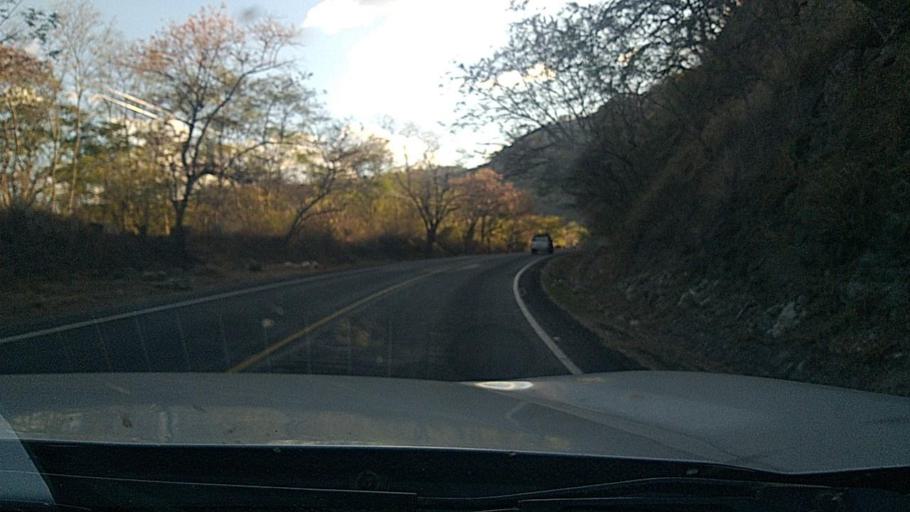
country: NI
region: Esteli
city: Condega
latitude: 13.2751
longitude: -86.3522
